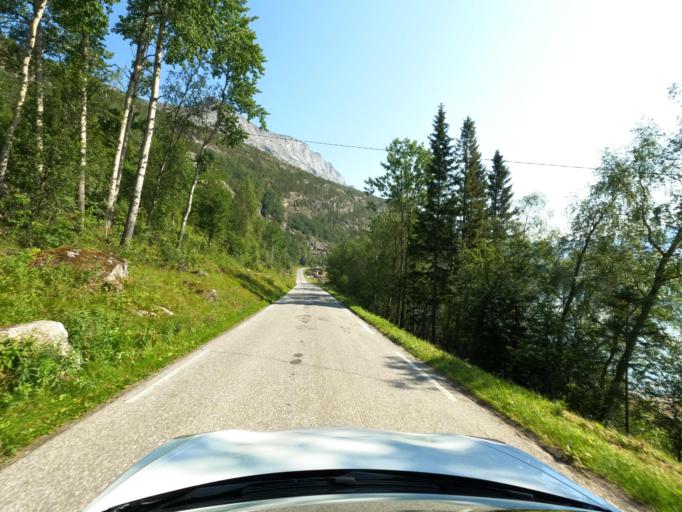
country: NO
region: Nordland
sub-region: Narvik
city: Narvik
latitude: 68.2758
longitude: 17.3919
